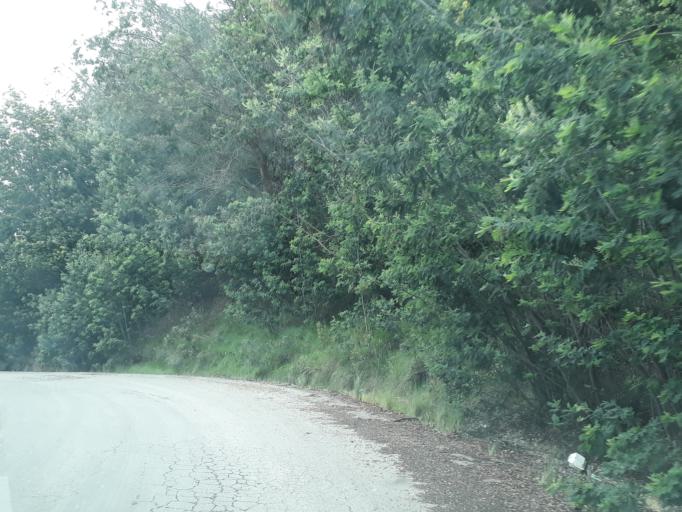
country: CO
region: Cundinamarca
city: Cucunuba
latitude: 5.2089
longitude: -73.7861
